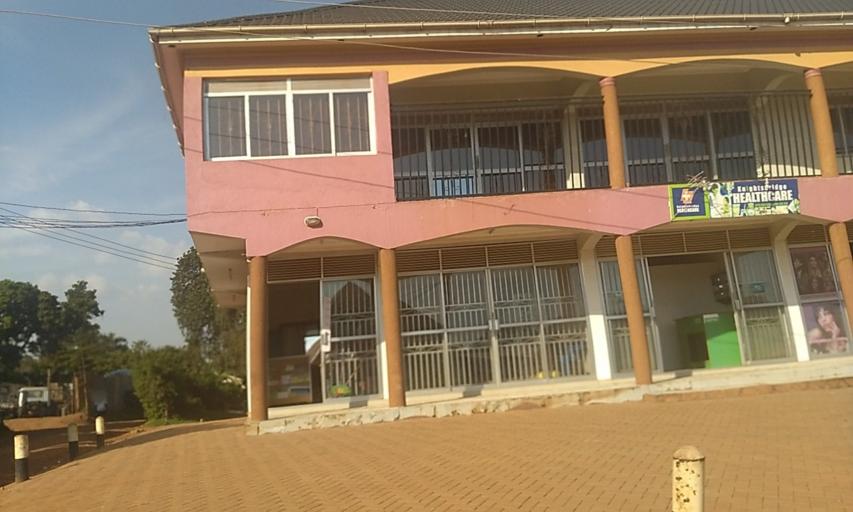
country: UG
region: Central Region
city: Kampala Central Division
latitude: 0.3205
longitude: 32.5465
